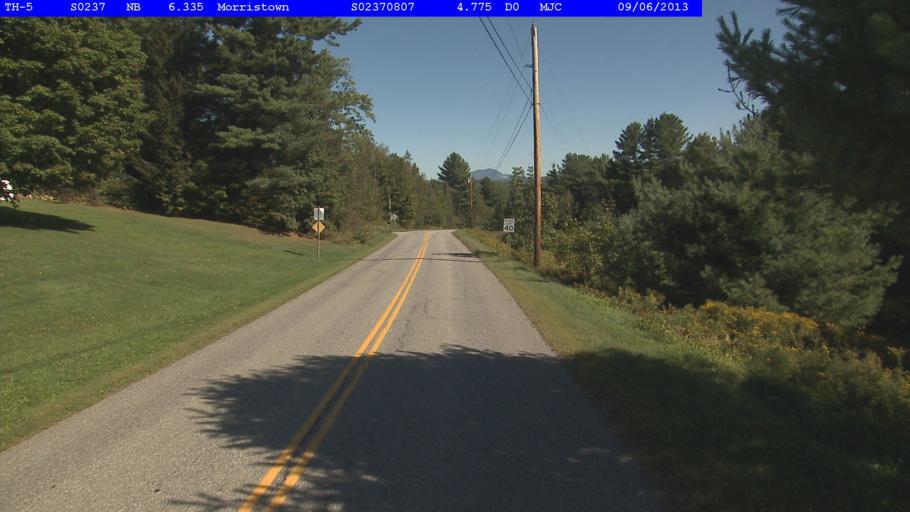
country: US
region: Vermont
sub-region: Lamoille County
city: Morristown
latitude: 44.5643
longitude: -72.6212
